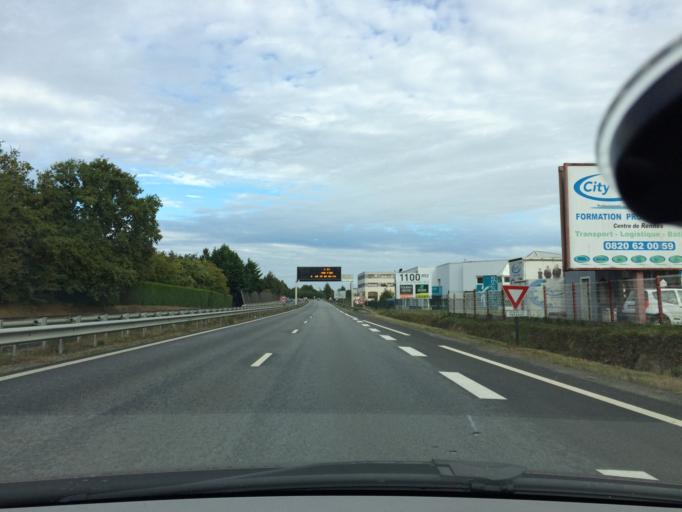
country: FR
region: Brittany
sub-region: Departement d'Ille-et-Vilaine
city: Chantepie
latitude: 48.0748
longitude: -1.6283
